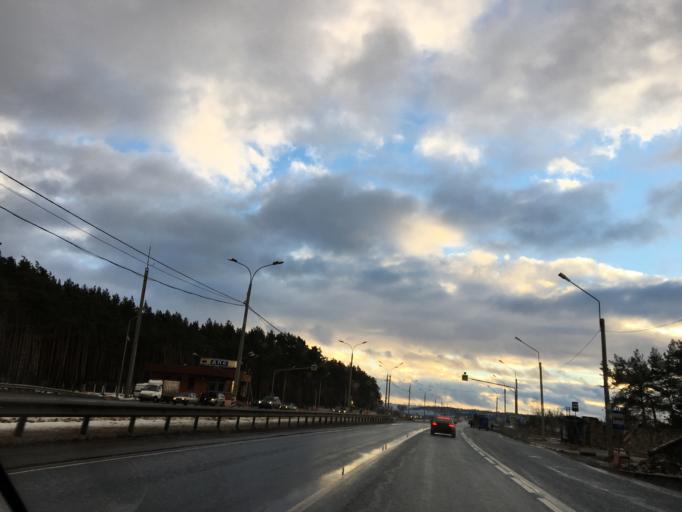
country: RU
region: Moskovskaya
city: Danki
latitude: 54.8834
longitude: 37.5109
